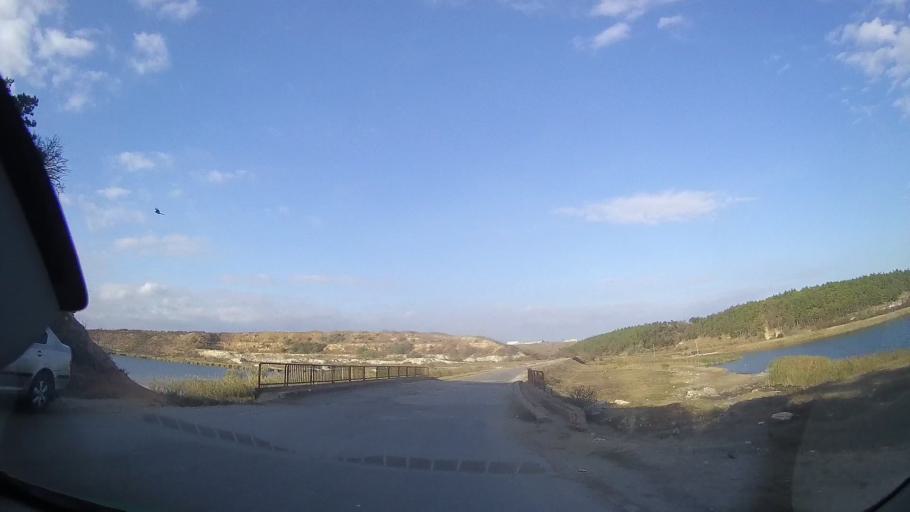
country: RO
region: Constanta
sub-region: Comuna Limanu
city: Limanu
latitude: 43.8122
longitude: 28.5168
